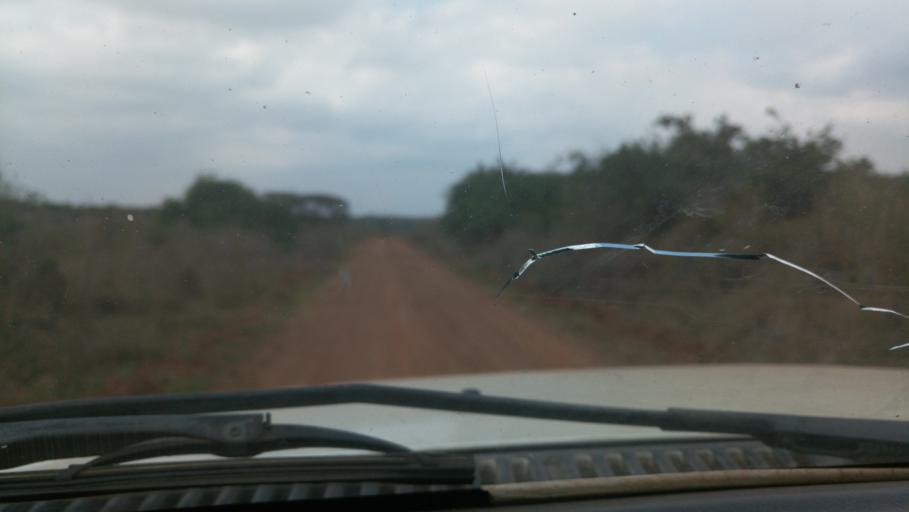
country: KE
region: Nairobi Area
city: Pumwani
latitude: -1.3748
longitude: 36.8405
